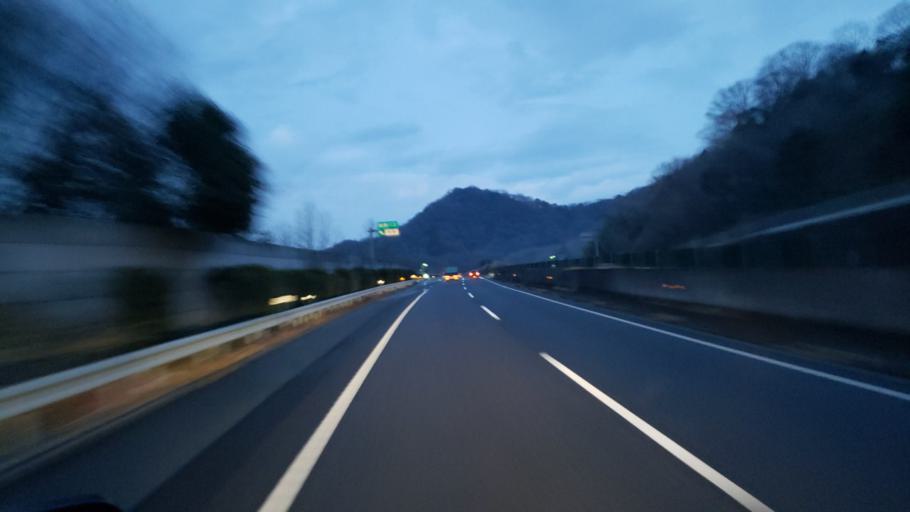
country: JP
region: Hyogo
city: Himeji
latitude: 34.8522
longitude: 134.7635
